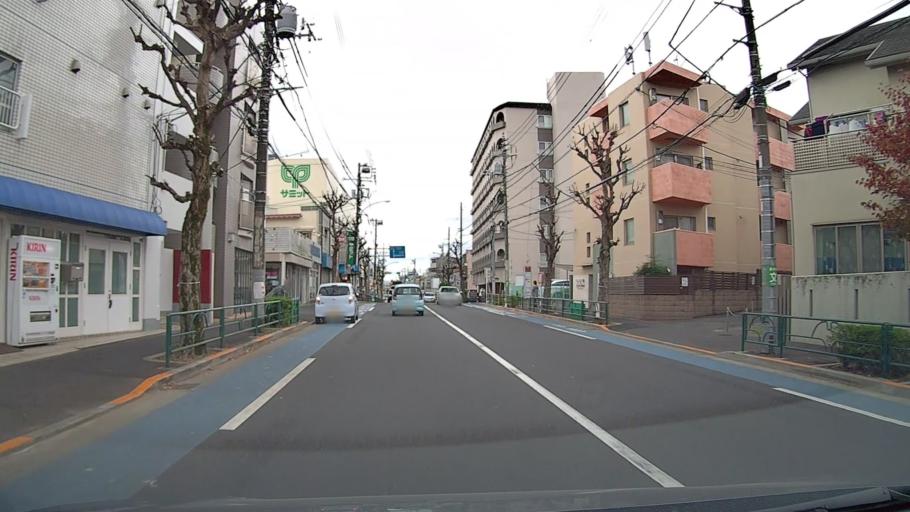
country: JP
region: Tokyo
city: Tokyo
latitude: 35.7160
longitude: 139.6286
